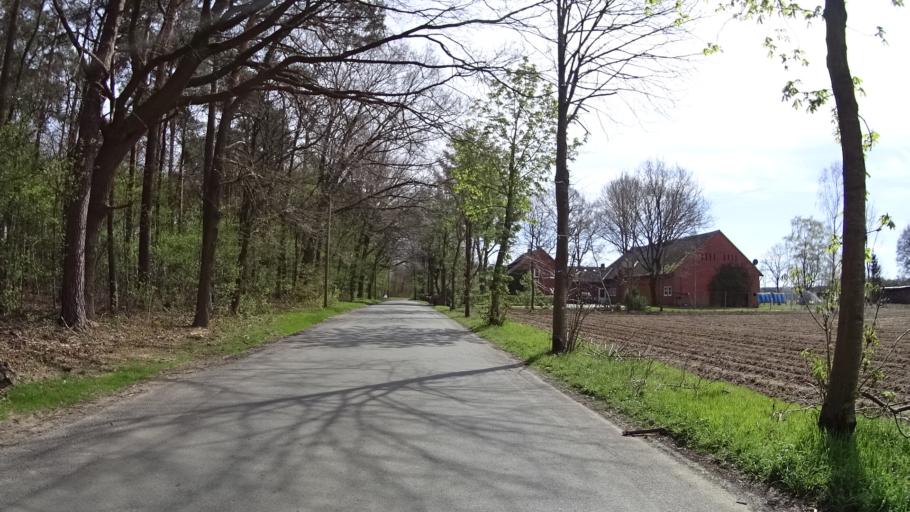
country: DE
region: Lower Saxony
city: Emsburen
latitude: 52.4313
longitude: 7.3519
